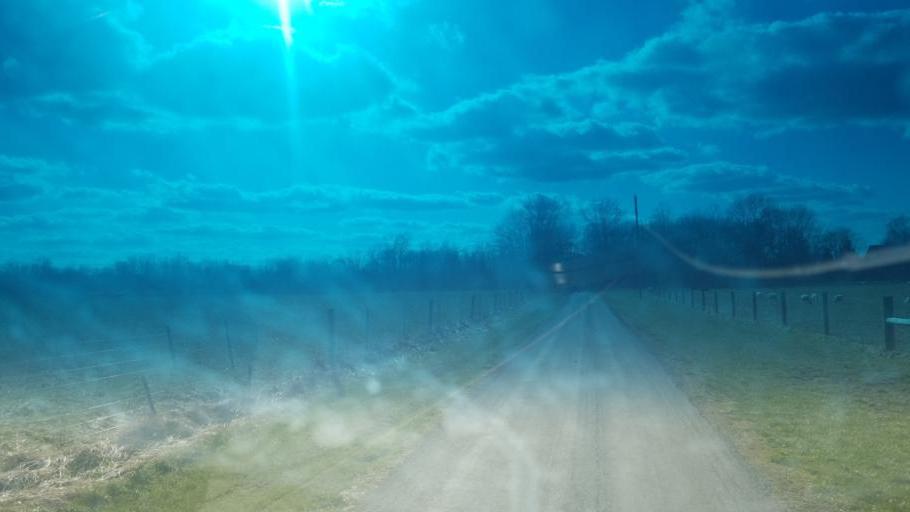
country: US
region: Ohio
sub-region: Highland County
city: Greenfield
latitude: 39.3171
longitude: -83.4074
